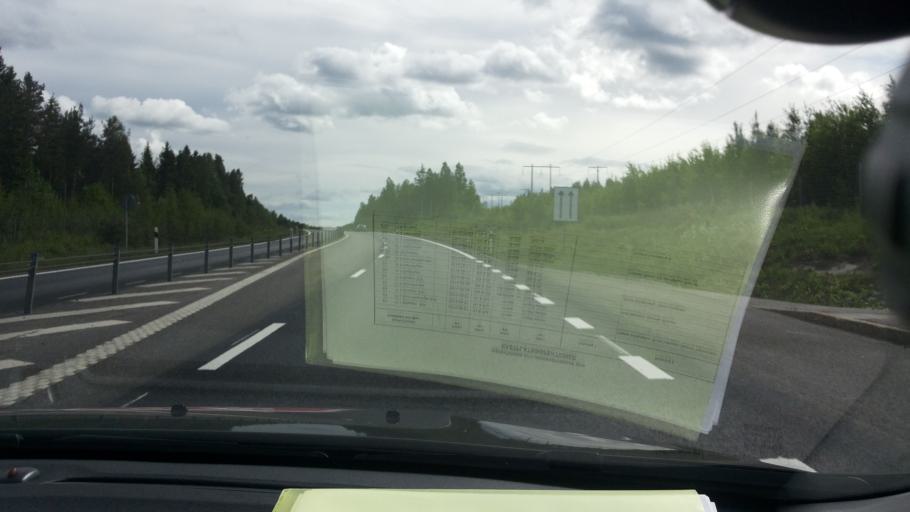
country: SE
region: Vaesternorrland
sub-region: Sundsvalls Kommun
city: Njurundabommen
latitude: 62.1848
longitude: 17.3564
